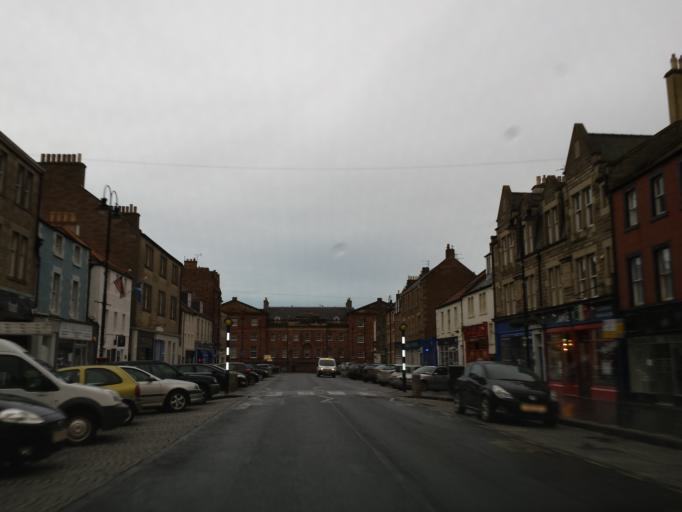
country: GB
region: Scotland
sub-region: East Lothian
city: Dunbar
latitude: 56.0026
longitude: -2.5164
